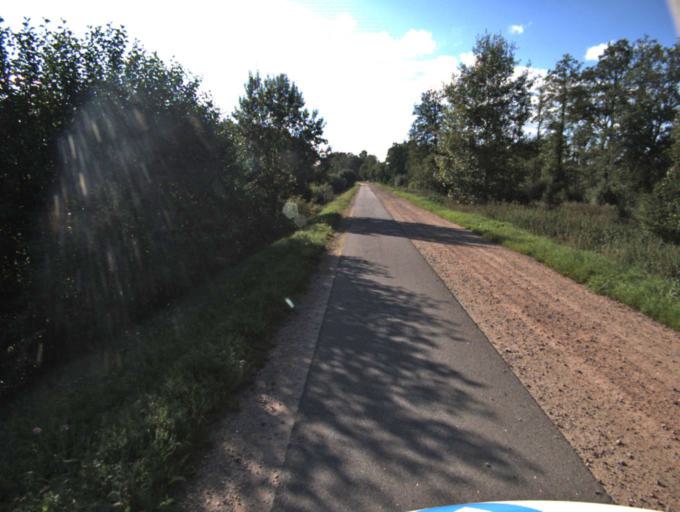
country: SE
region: Vaestra Goetaland
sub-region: Boras Kommun
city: Dalsjofors
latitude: 57.8250
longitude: 13.1667
